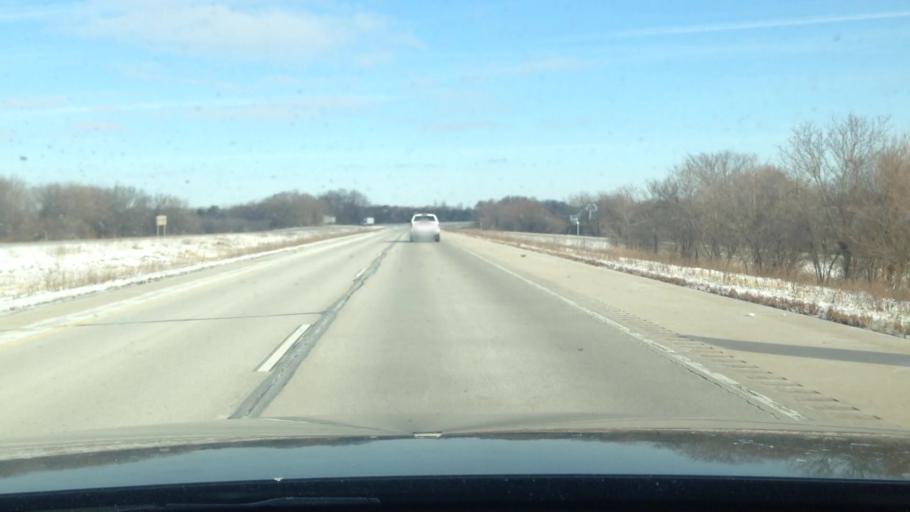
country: US
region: Wisconsin
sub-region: Walworth County
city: East Troy
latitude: 42.7938
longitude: -88.3841
